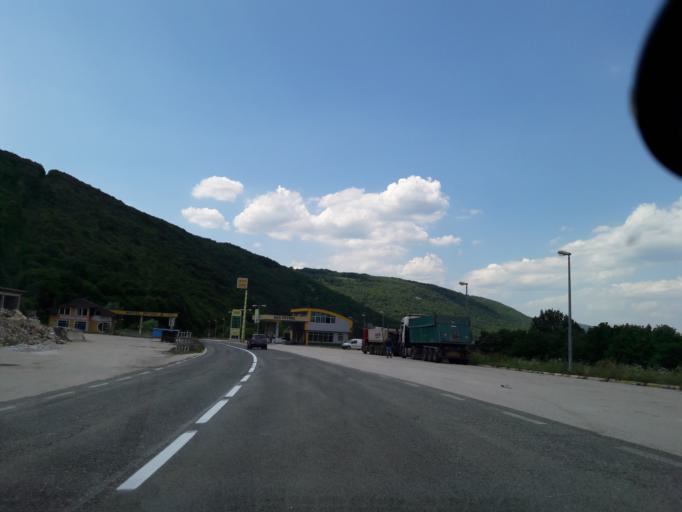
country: BA
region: Republika Srpska
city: Mrkonjic Grad
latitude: 44.4884
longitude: 17.1606
